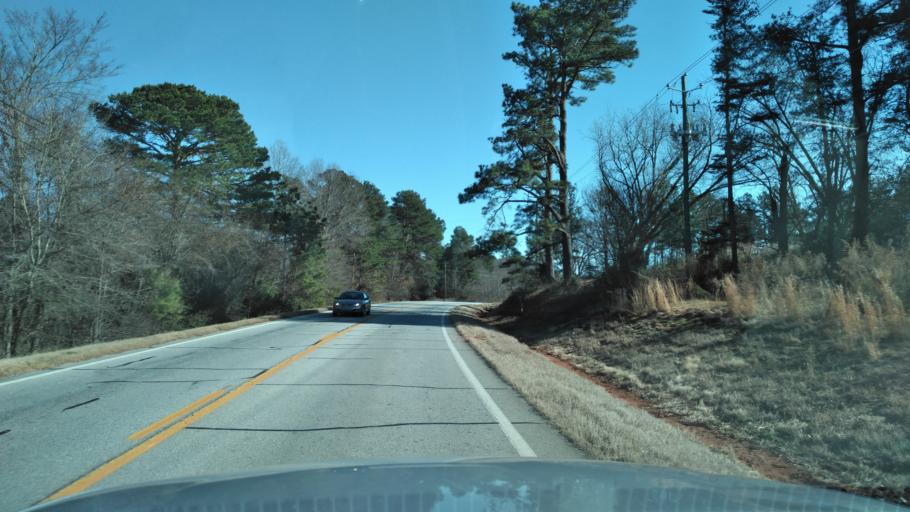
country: US
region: Georgia
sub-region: Jackson County
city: Commerce
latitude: 34.2331
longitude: -83.5025
